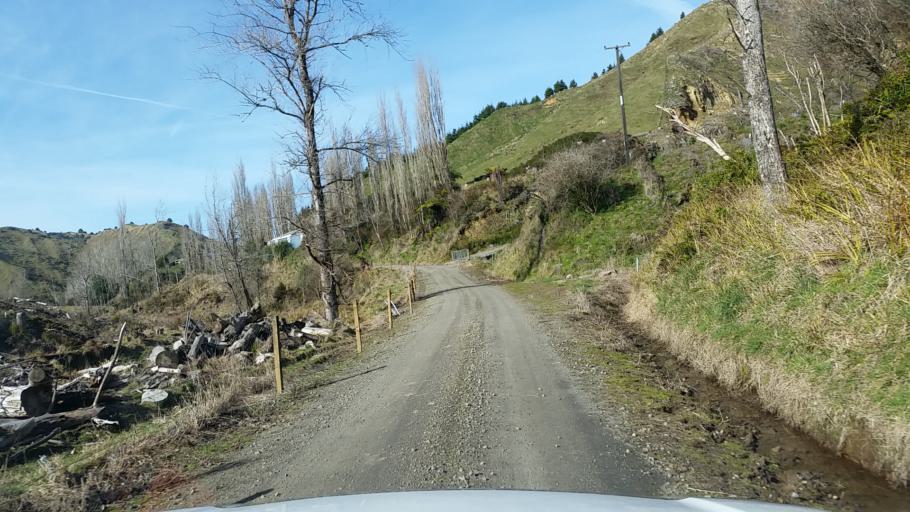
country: NZ
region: Taranaki
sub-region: South Taranaki District
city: Eltham
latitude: -39.3648
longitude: 174.5170
